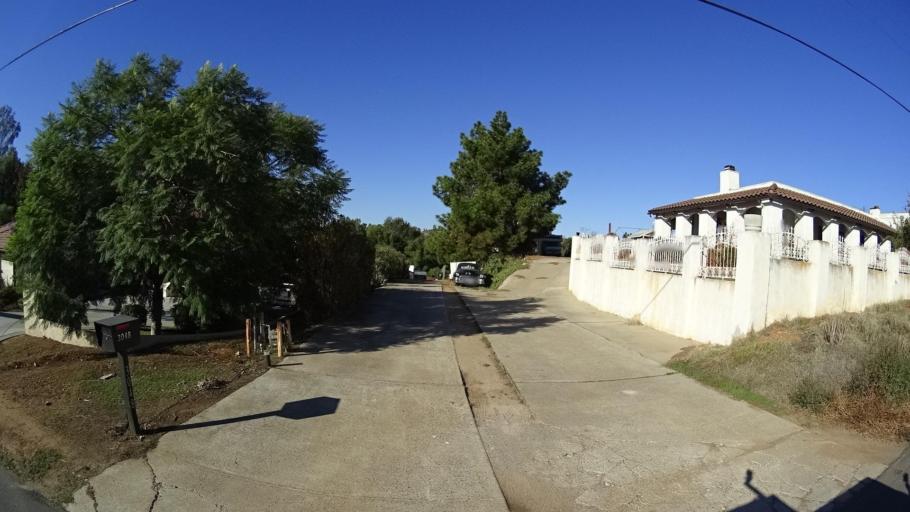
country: US
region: California
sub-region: San Diego County
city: Bonita
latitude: 32.6789
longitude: -117.0222
